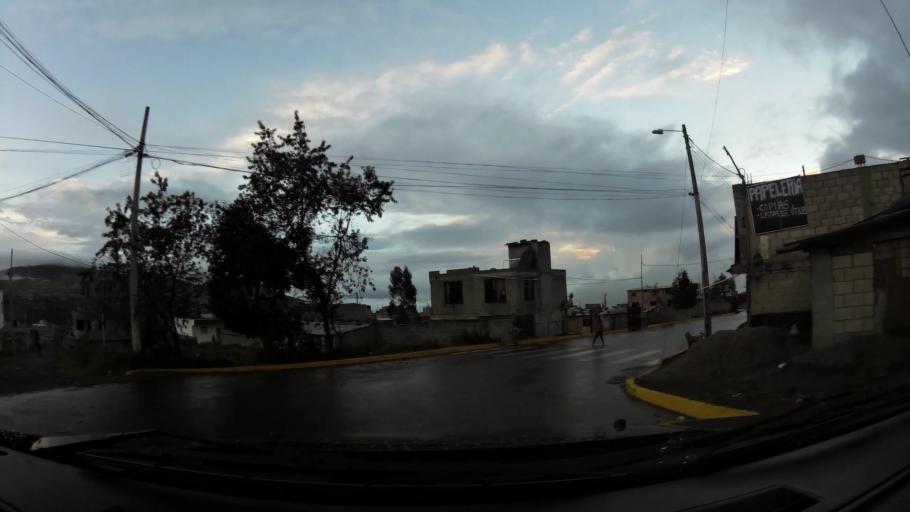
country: EC
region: Pichincha
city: Quito
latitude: -0.0960
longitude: -78.5302
